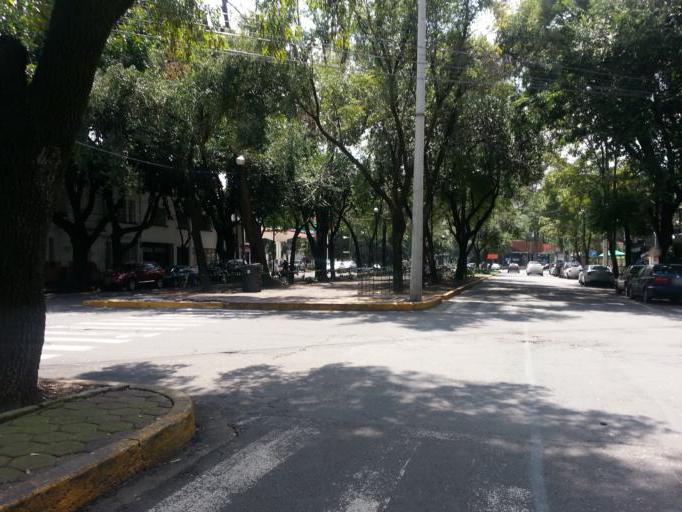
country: MX
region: Mexico City
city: Benito Juarez
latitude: 19.4184
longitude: -99.1738
